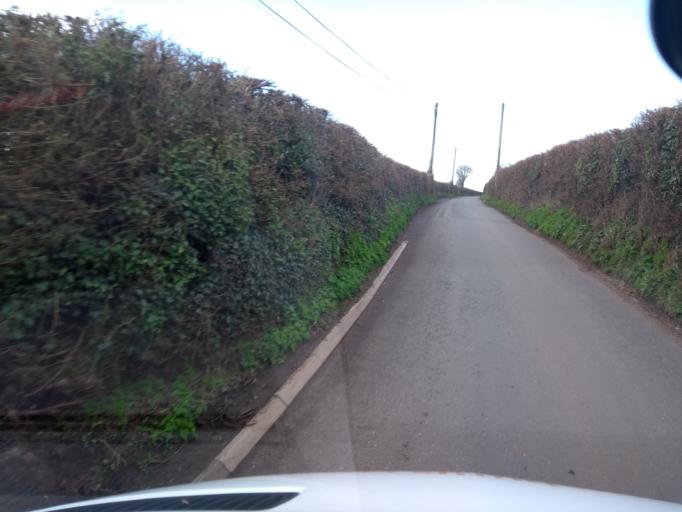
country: GB
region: England
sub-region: Somerset
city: Westonzoyland
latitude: 51.1236
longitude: -2.8469
